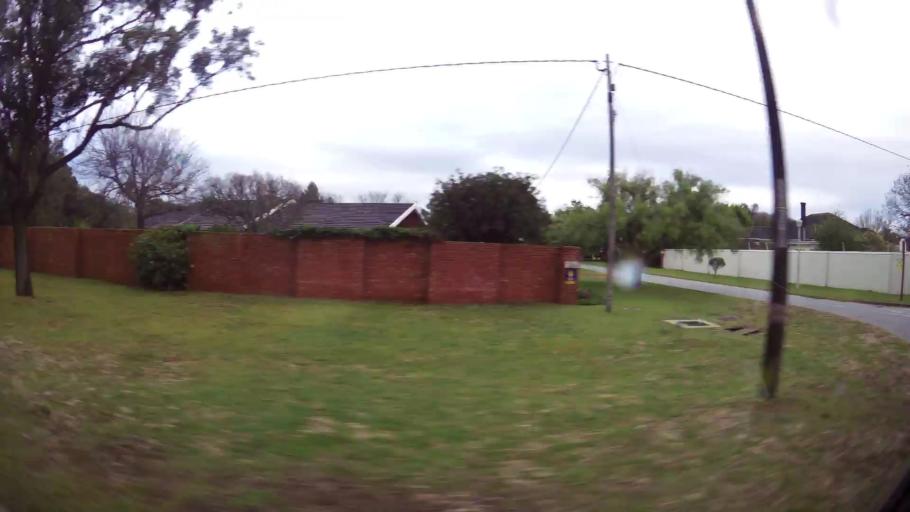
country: ZA
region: Eastern Cape
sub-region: Nelson Mandela Bay Metropolitan Municipality
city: Port Elizabeth
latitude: -33.9795
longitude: 25.5714
